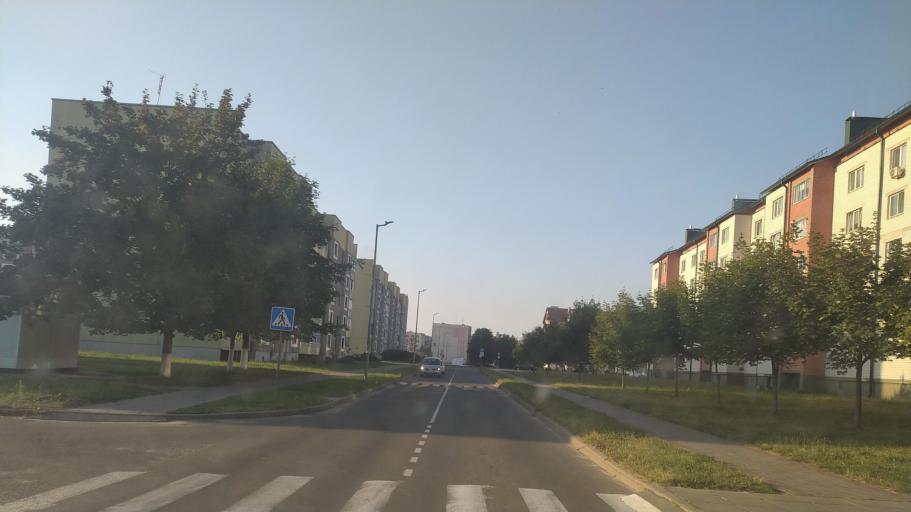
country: BY
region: Brest
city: Byaroza
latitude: 52.5461
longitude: 24.9843
